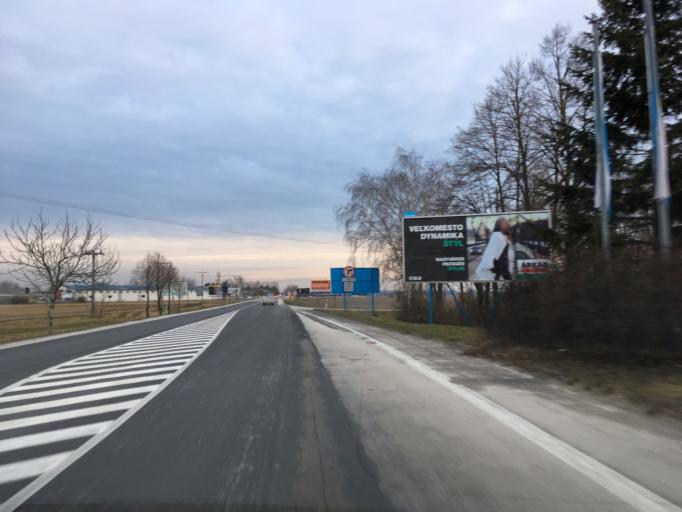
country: SK
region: Trnavsky
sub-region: Okres Dunajska Streda
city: Velky Meder
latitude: 47.9362
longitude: 17.7197
